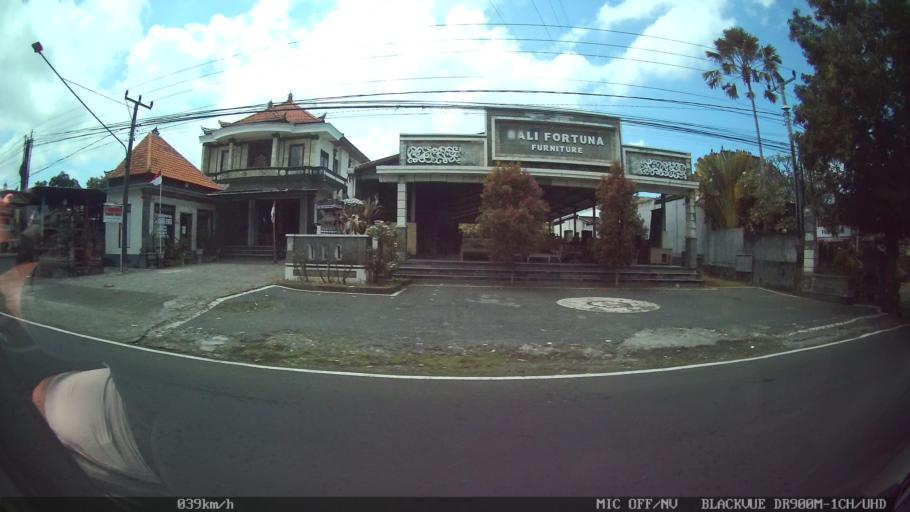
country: ID
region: Bali
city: Banjar Desa
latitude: -8.5759
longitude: 115.2766
